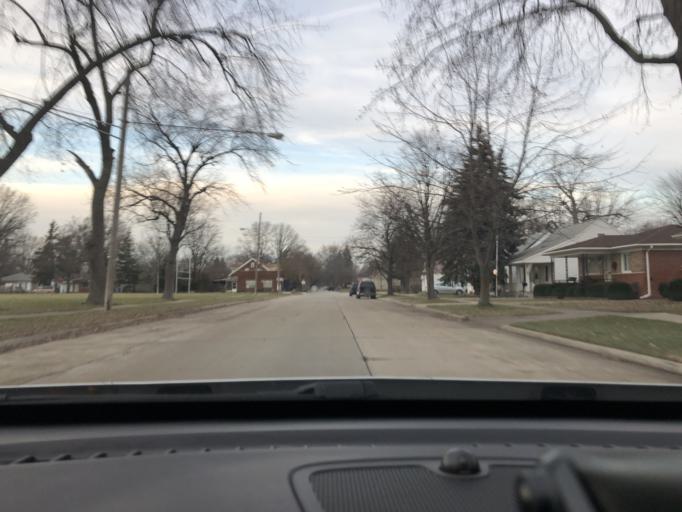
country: US
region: Michigan
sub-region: Wayne County
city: Allen Park
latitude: 42.2760
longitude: -83.2362
